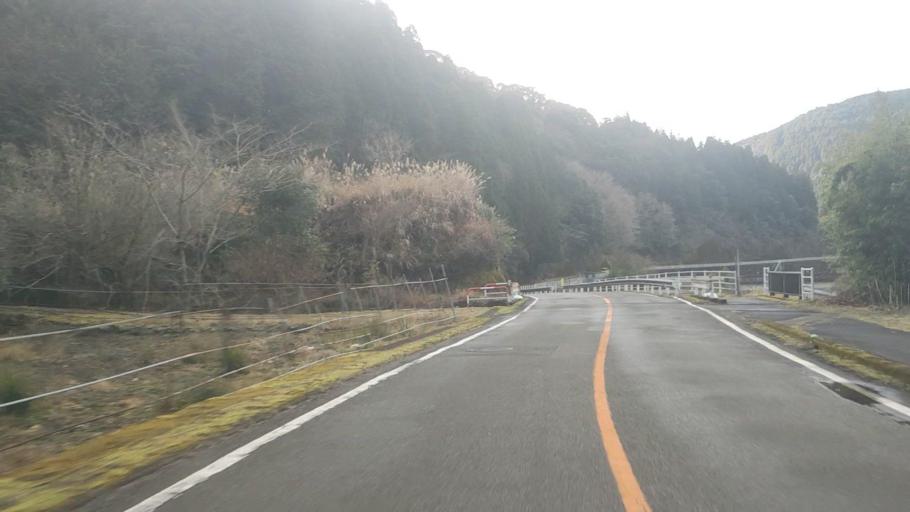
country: JP
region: Kumamoto
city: Hitoyoshi
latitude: 32.2958
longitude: 130.8464
